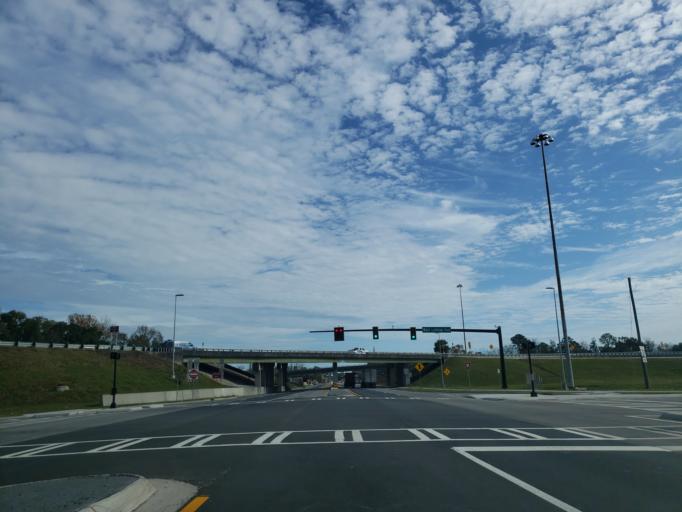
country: US
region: Georgia
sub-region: Chatham County
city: Savannah
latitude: 32.0912
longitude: -81.1292
